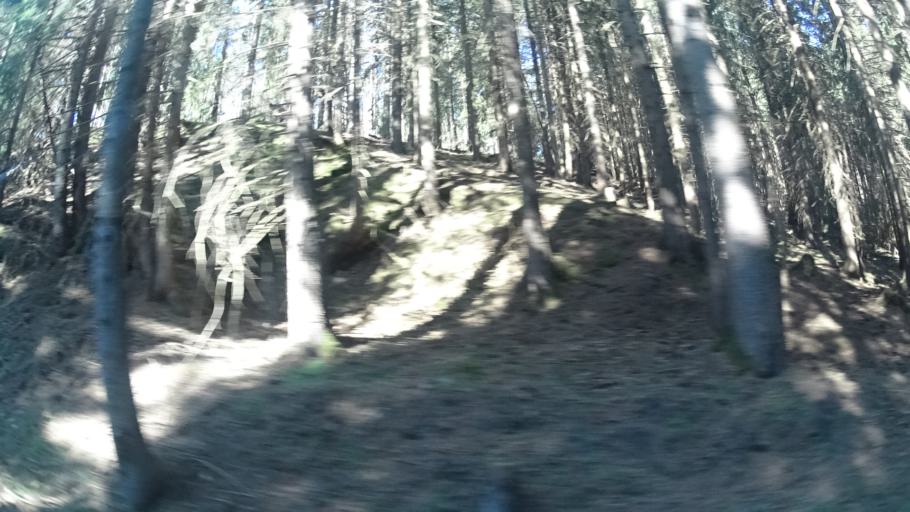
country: DE
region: Thuringia
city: Wildenspring
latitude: 50.5755
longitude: 11.0623
